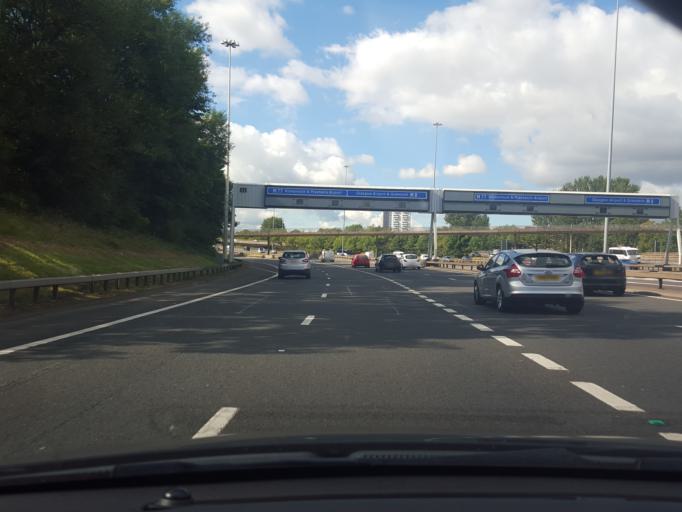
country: GB
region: Scotland
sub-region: Glasgow City
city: Glasgow
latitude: 55.8500
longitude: -4.2897
